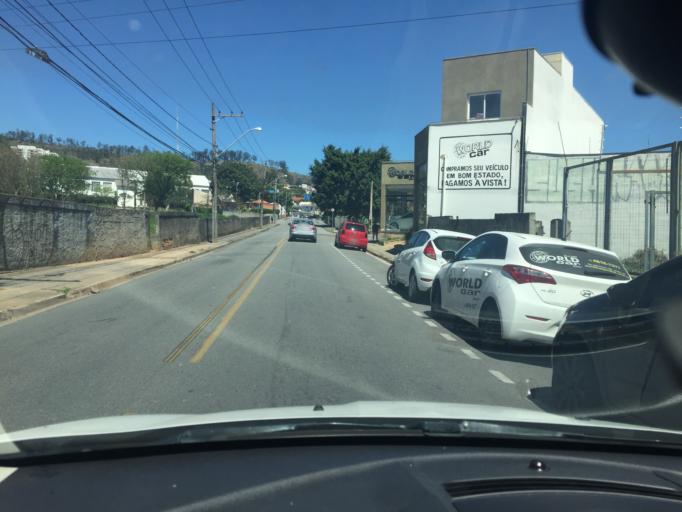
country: BR
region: Sao Paulo
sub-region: Jundiai
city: Jundiai
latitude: -23.2055
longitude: -46.8830
